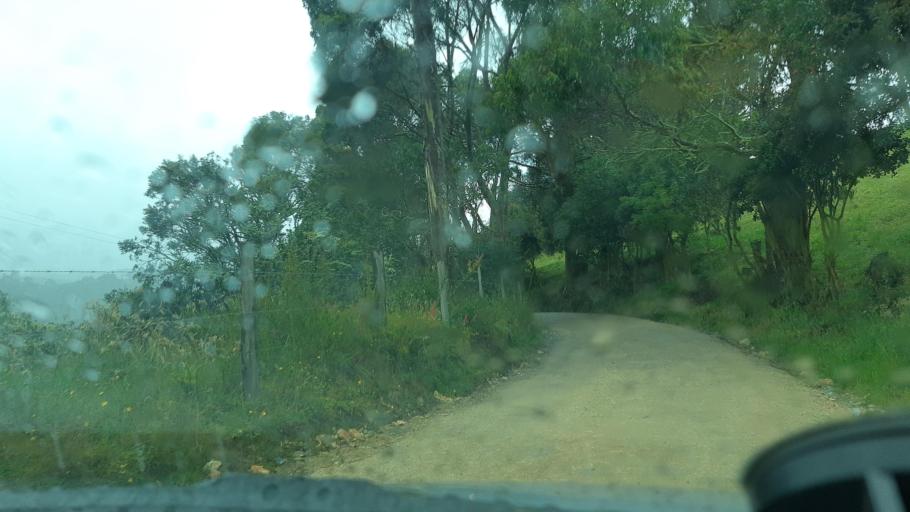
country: CO
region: Cundinamarca
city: Villapinzon
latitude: 5.2101
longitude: -73.5711
